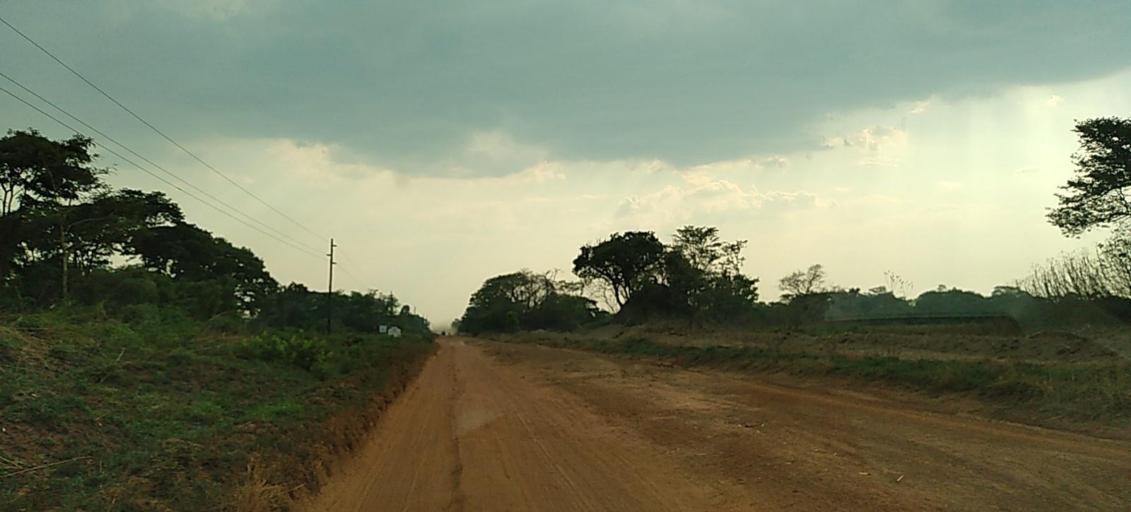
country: ZM
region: Copperbelt
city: Kalulushi
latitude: -12.9404
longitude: 27.9234
